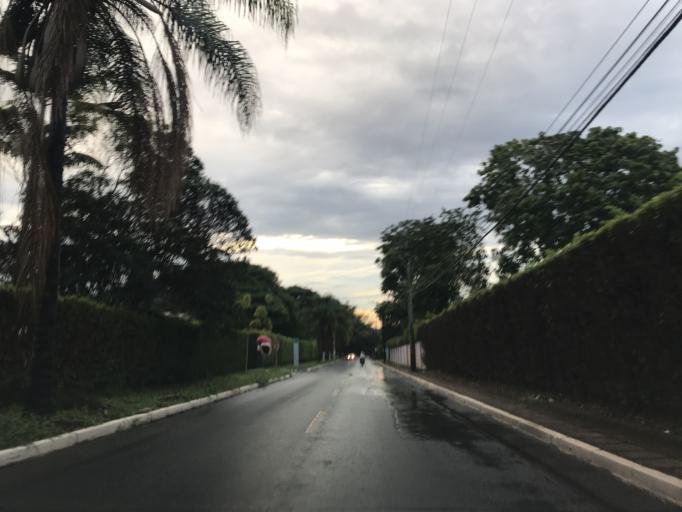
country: BR
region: Federal District
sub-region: Brasilia
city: Brasilia
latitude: -15.8534
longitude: -47.8547
